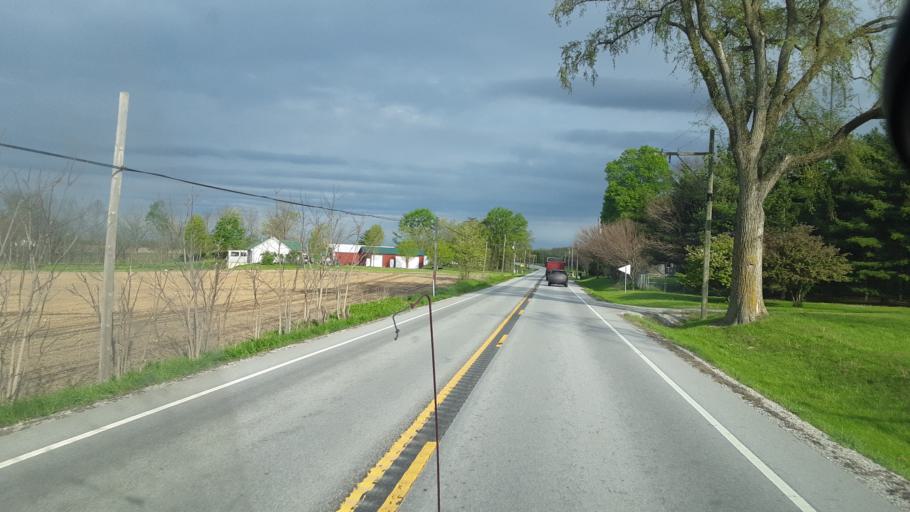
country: US
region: Indiana
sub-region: Whitley County
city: Tri-Lakes
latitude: 41.2599
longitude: -85.3782
